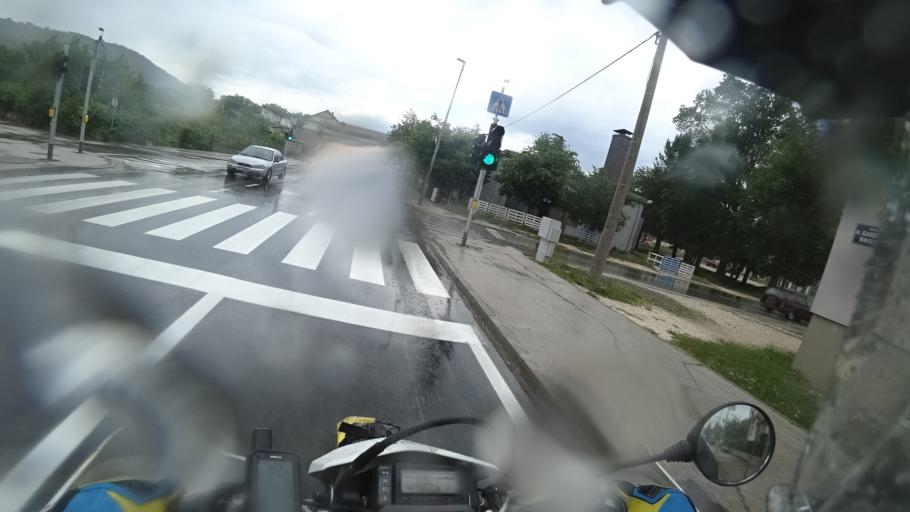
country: HR
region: Sibensko-Kniniska
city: Knin
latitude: 44.0403
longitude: 16.2021
